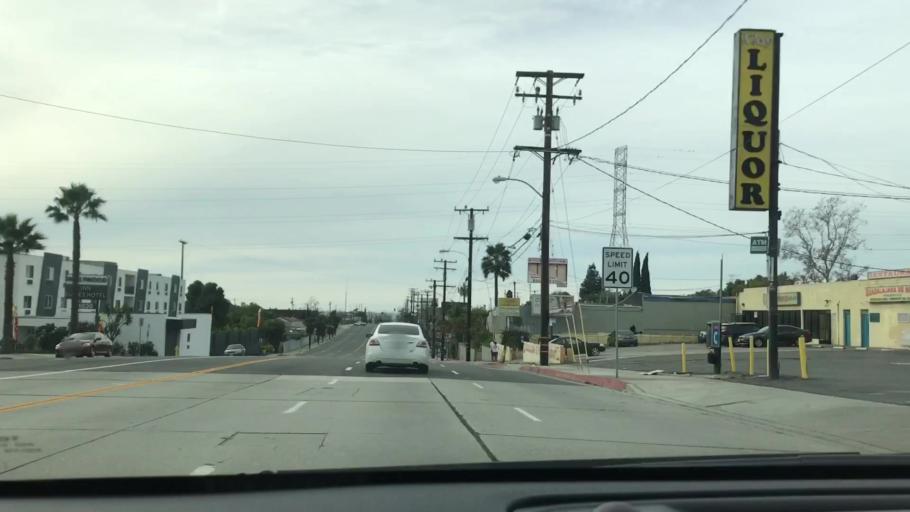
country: US
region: California
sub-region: Los Angeles County
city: West Athens
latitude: 33.9165
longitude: -118.2923
